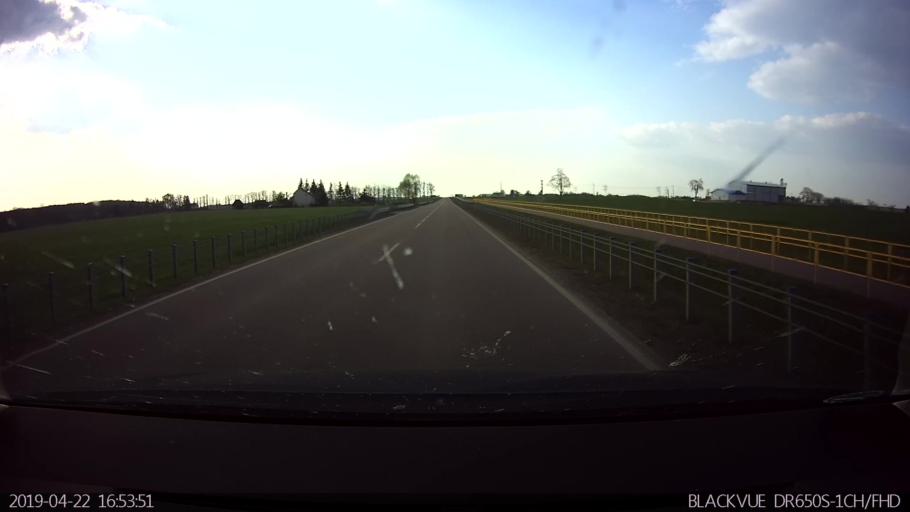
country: PL
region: Podlasie
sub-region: Powiat siemiatycki
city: Siemiatycze
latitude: 52.4576
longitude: 22.8263
